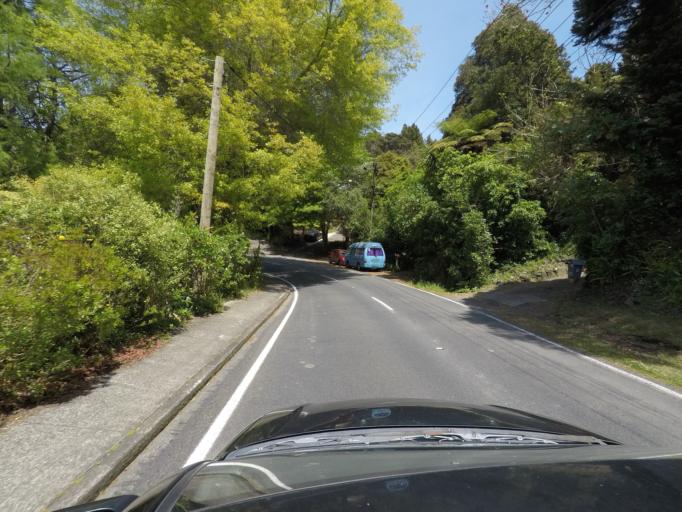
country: NZ
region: Auckland
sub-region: Auckland
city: Titirangi
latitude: -36.9598
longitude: 174.6418
